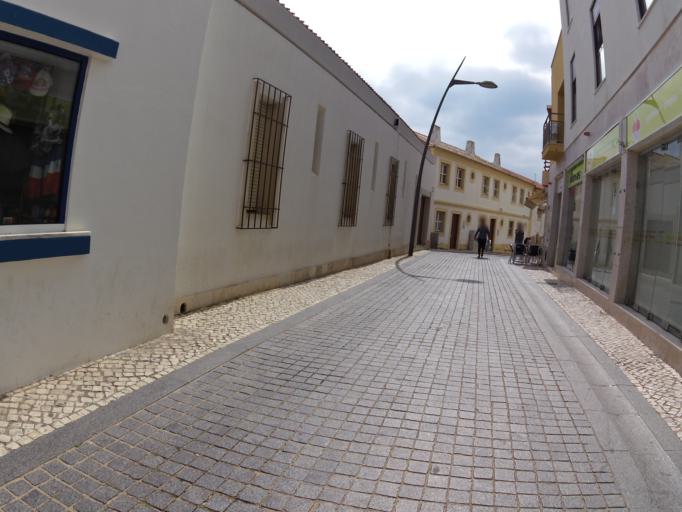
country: PT
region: Faro
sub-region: Silves
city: Armacao de Pera
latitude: 37.1011
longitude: -8.3594
